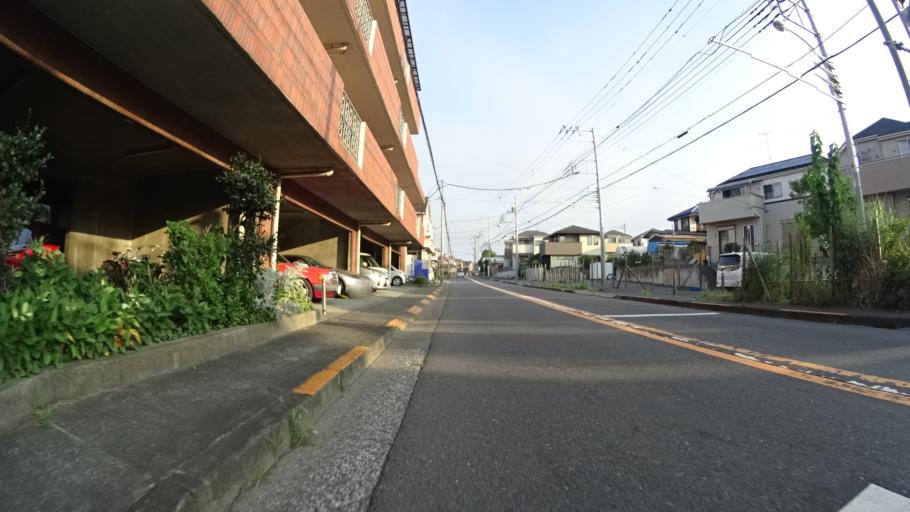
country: JP
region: Tokyo
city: Fussa
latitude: 35.7619
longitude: 139.3025
